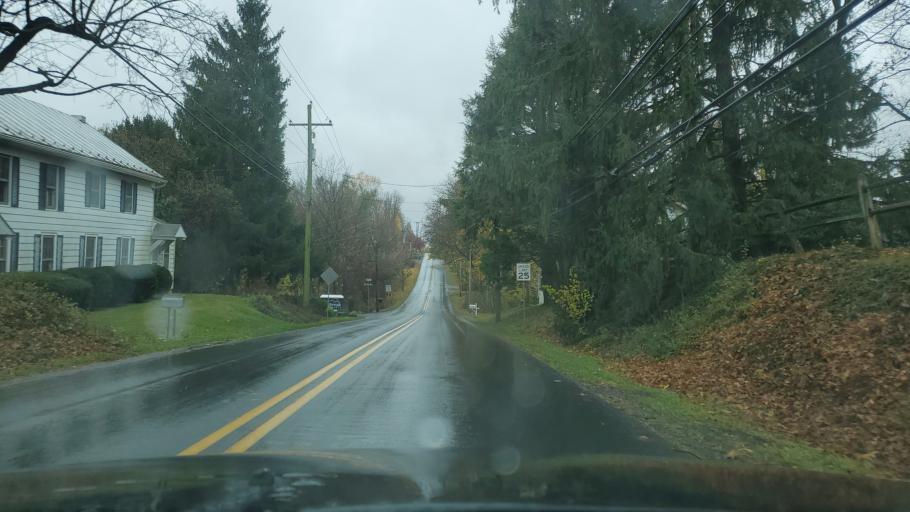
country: US
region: Pennsylvania
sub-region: Cumberland County
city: Mechanicsburg
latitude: 40.1774
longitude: -76.9916
